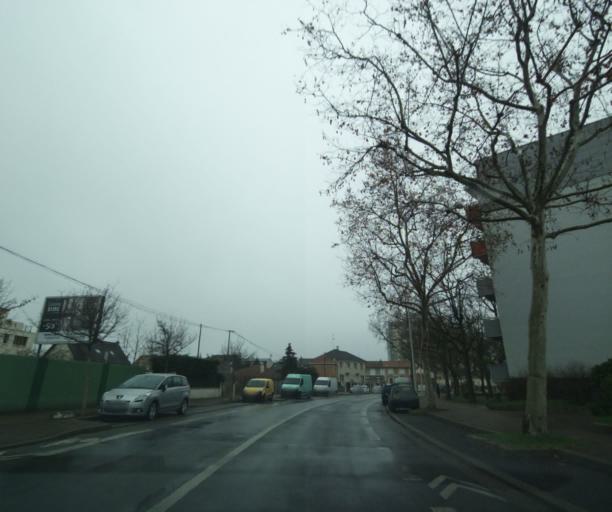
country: FR
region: Ile-de-France
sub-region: Departement des Hauts-de-Seine
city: Nanterre
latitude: 48.8966
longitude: 2.2073
